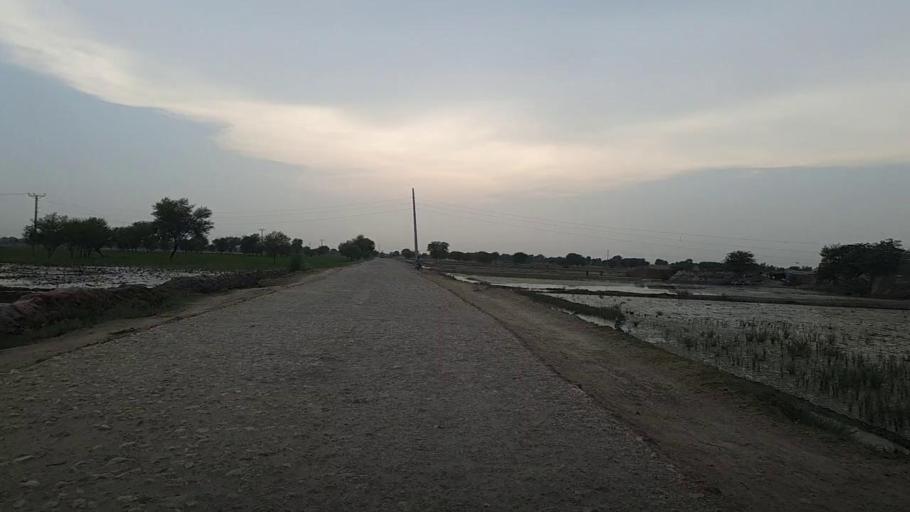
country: PK
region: Sindh
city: Khanpur
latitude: 27.8488
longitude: 69.4429
